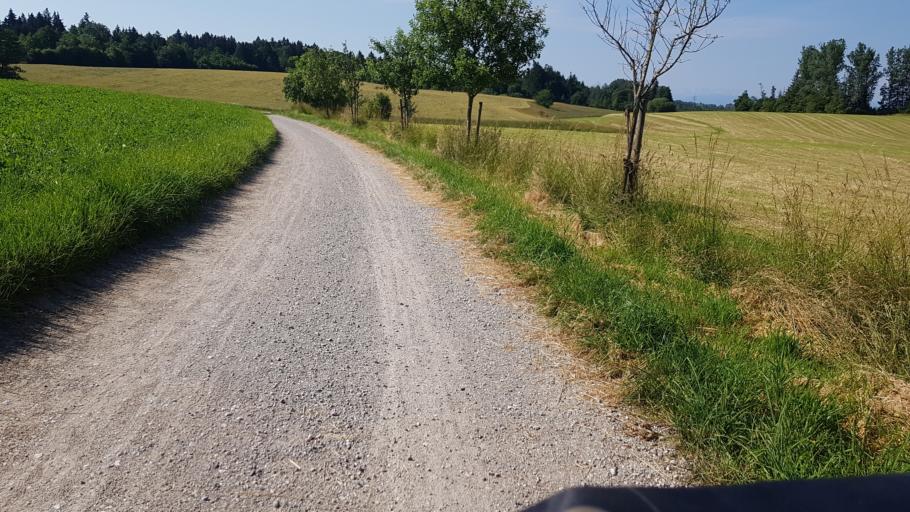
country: DE
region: Bavaria
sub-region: Upper Bavaria
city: Starnberg
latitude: 48.0238
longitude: 11.3714
